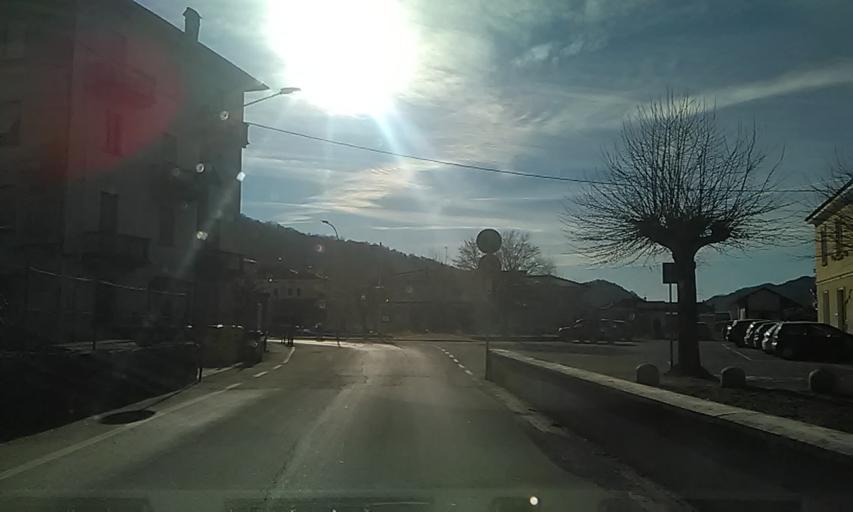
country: IT
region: Piedmont
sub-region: Provincia di Vercelli
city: Quarona
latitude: 45.7638
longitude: 8.2671
